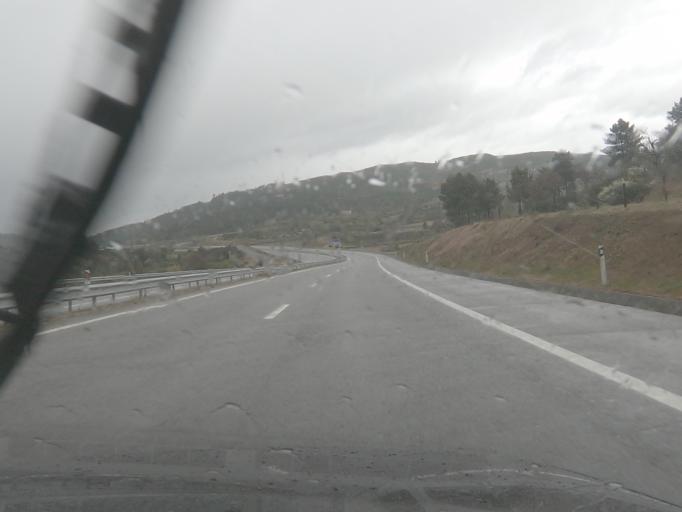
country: PT
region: Vila Real
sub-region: Boticas
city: Boticas
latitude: 41.6615
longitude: -7.5741
